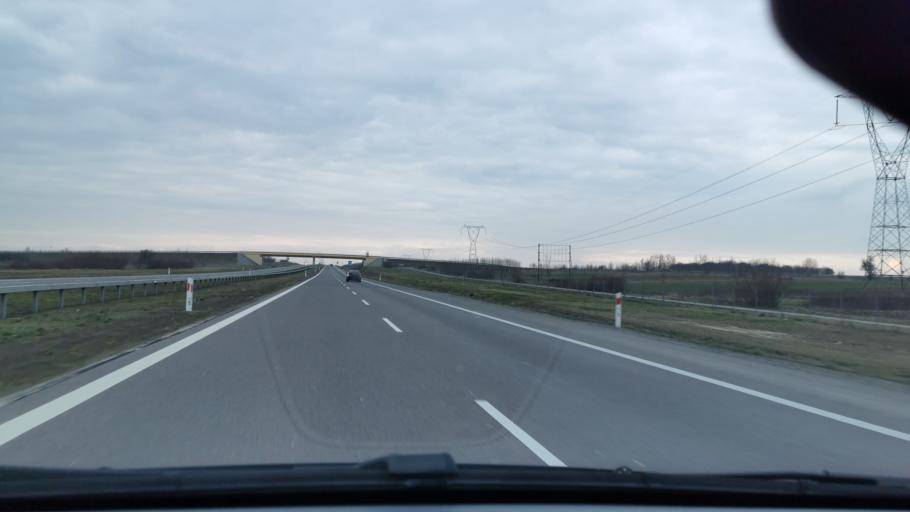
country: PL
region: Lublin Voivodeship
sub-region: Powiat pulawski
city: Markuszow
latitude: 51.3856
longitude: 22.2666
